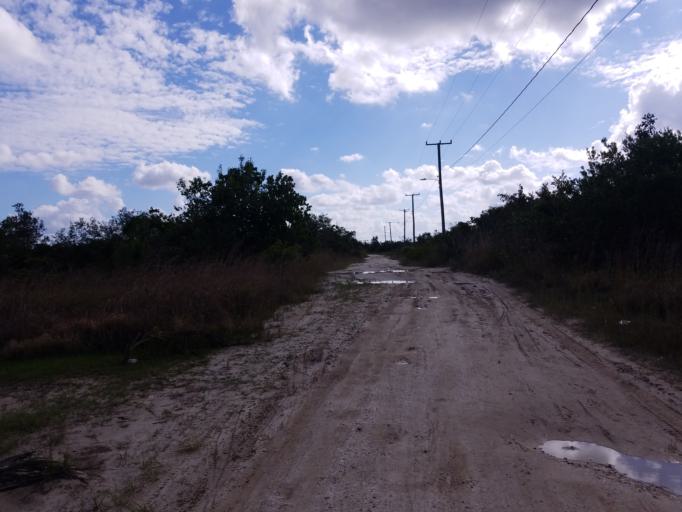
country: BZ
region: Belize
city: Belize City
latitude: 17.5667
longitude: -88.4111
